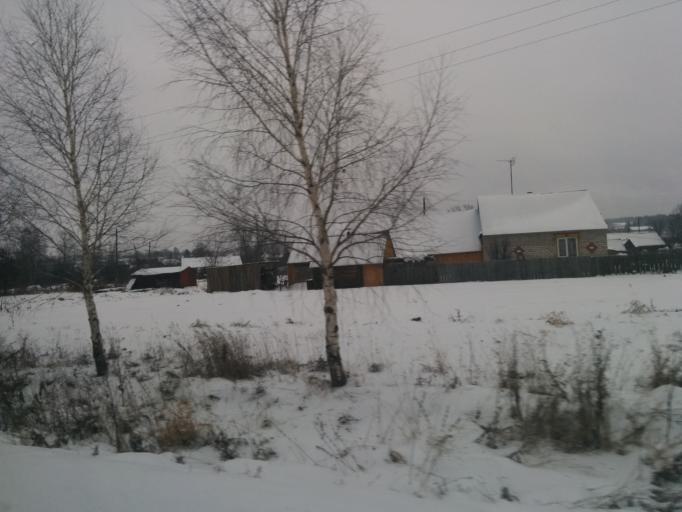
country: RU
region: Perm
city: Okhansk
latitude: 57.5193
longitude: 55.2581
